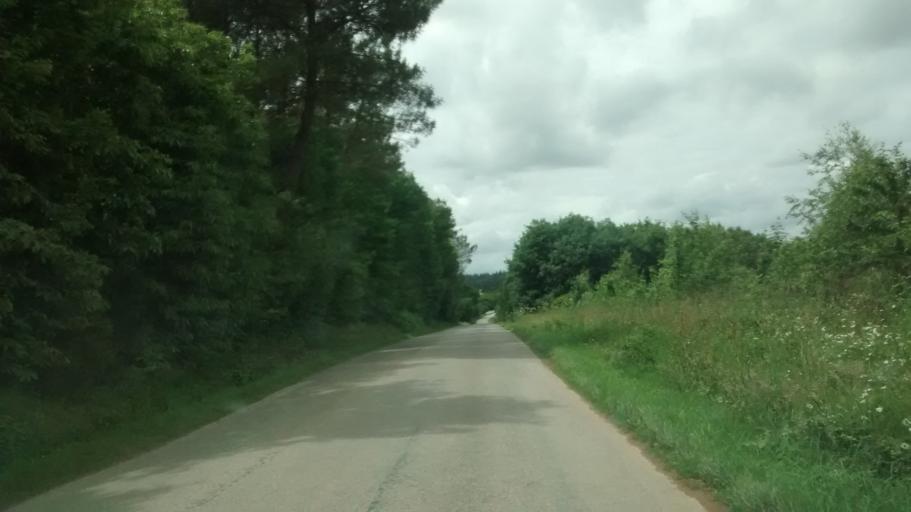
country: FR
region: Brittany
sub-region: Departement du Morbihan
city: Carentoir
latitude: 47.8226
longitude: -2.1573
